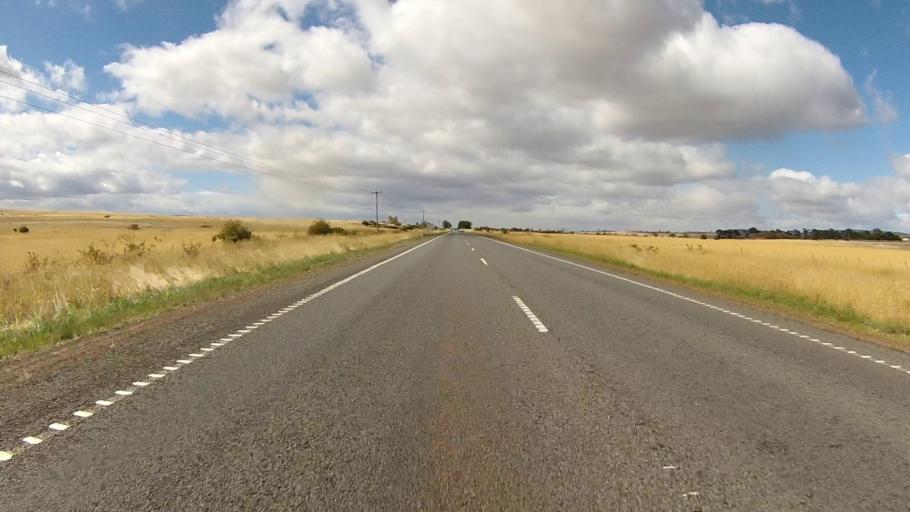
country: AU
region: Tasmania
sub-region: Northern Midlands
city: Evandale
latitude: -41.8566
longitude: 147.4538
